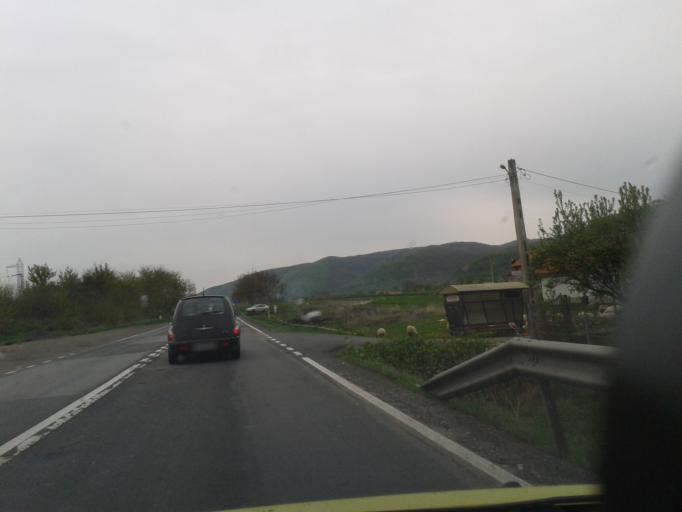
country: RO
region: Hunedoara
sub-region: Comuna Branisca
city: Branisca
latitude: 45.9036
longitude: 22.7900
